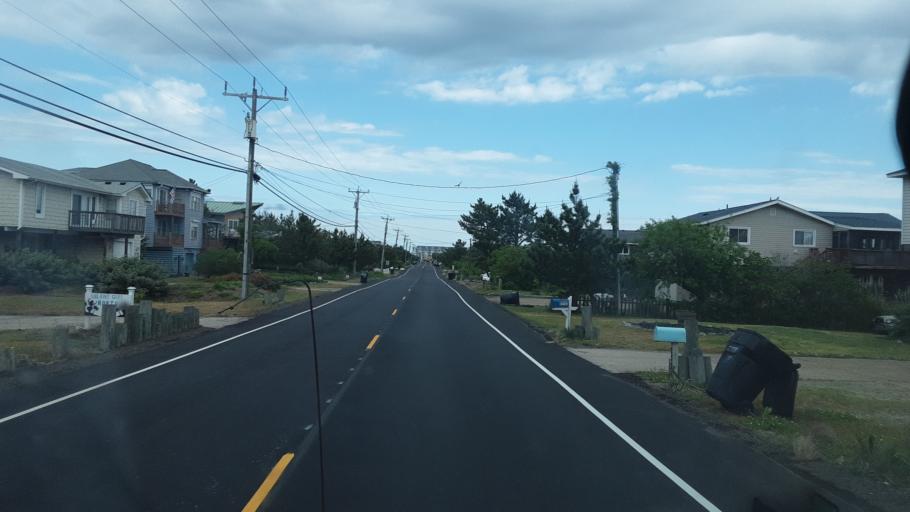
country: US
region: Virginia
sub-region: City of Virginia Beach
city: Virginia Beach
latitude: 36.7370
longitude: -75.9418
